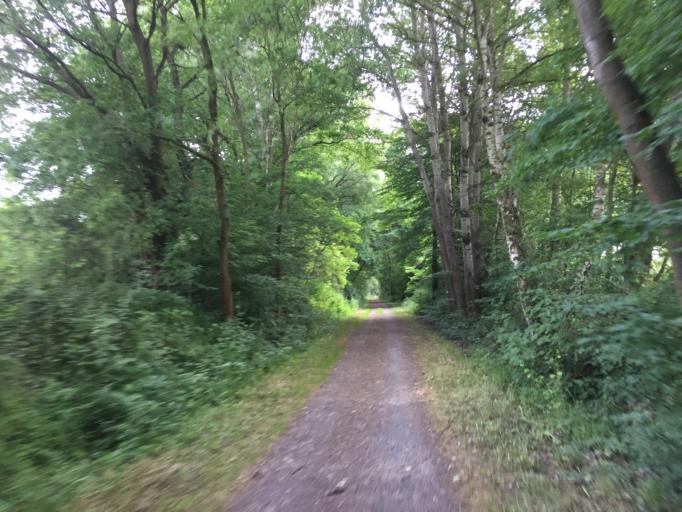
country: DE
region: Hesse
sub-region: Regierungsbezirk Kassel
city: Lohfelden
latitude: 51.2484
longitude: 9.5548
